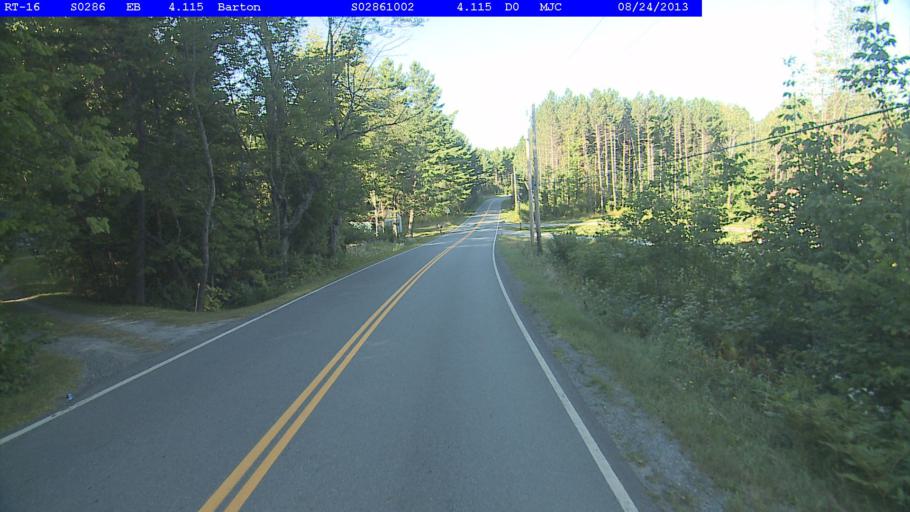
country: US
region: Vermont
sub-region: Orleans County
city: Newport
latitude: 44.7803
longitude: -72.1241
